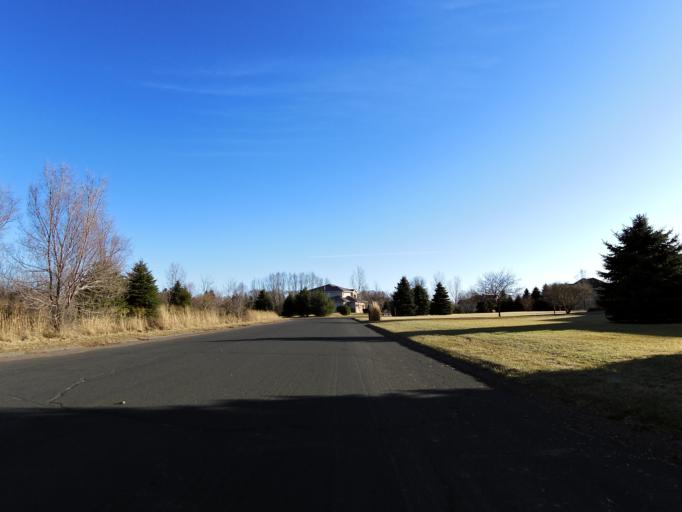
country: US
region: Minnesota
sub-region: Washington County
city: Lakeland
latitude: 44.9706
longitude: -92.8047
